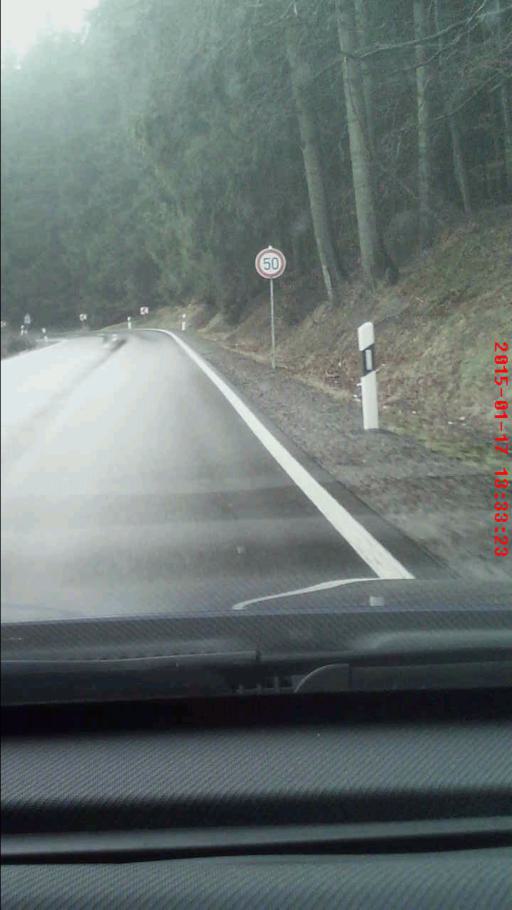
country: DE
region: Thuringia
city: Grossbreitenbach
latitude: 50.6036
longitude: 10.9855
